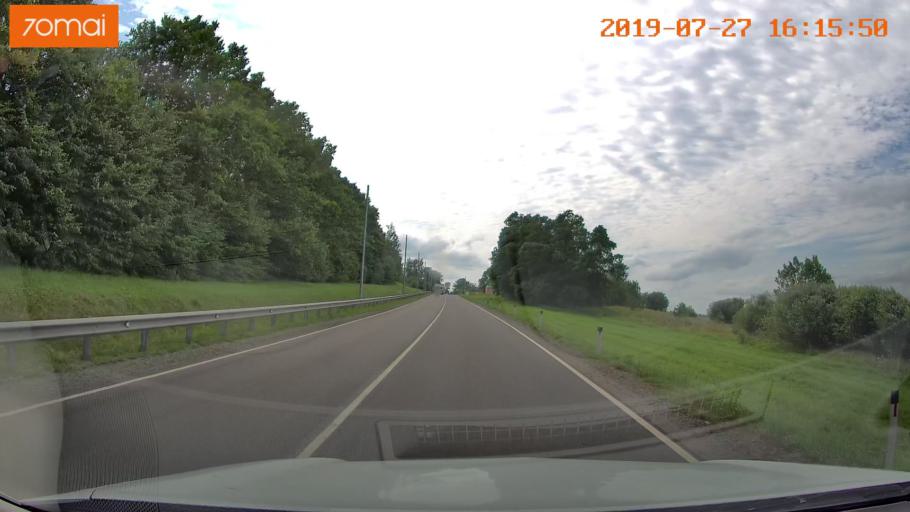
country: RU
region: Kaliningrad
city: Chernyakhovsk
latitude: 54.6250
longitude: 21.5853
